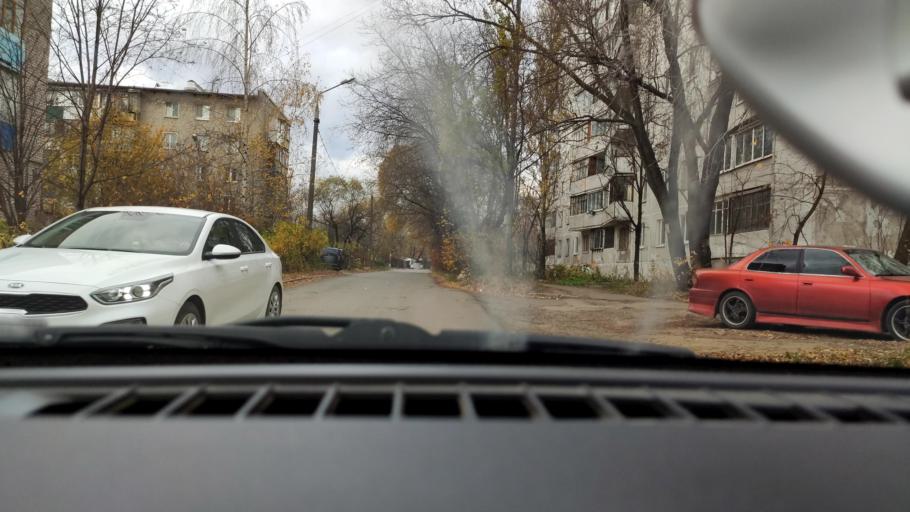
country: RU
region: Perm
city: Perm
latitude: 57.9617
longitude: 56.2262
